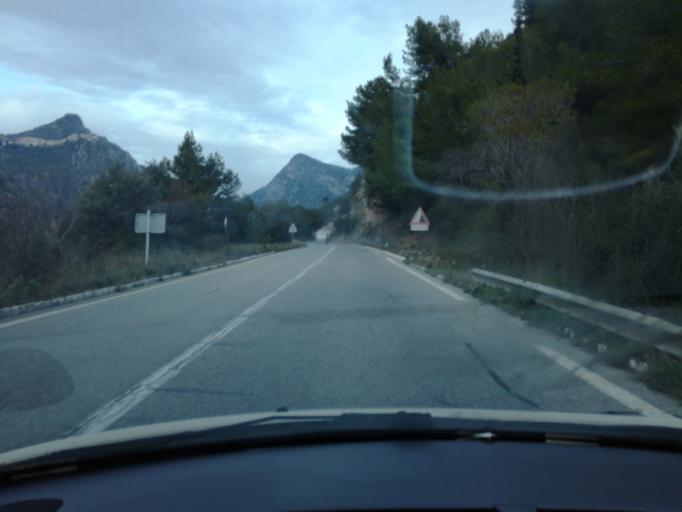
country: FR
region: Provence-Alpes-Cote d'Azur
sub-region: Departement des Alpes-Maritimes
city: Saint-Martin-du-Var
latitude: 43.8473
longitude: 7.1977
